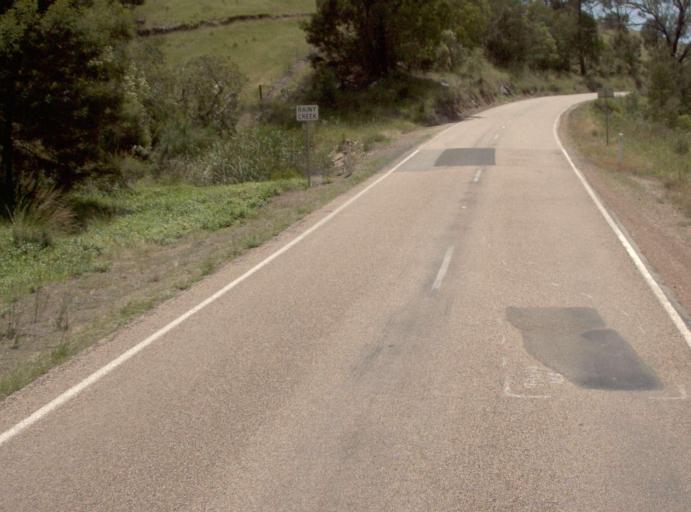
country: AU
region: Victoria
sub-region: East Gippsland
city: Bairnsdale
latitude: -37.5259
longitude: 147.8435
